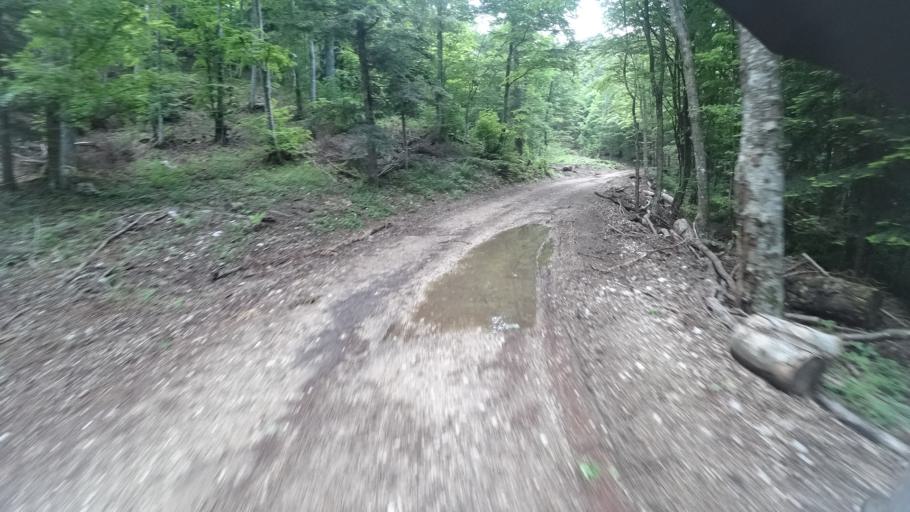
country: BA
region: Federation of Bosnia and Herzegovina
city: Izacic
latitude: 44.7581
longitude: 15.7643
